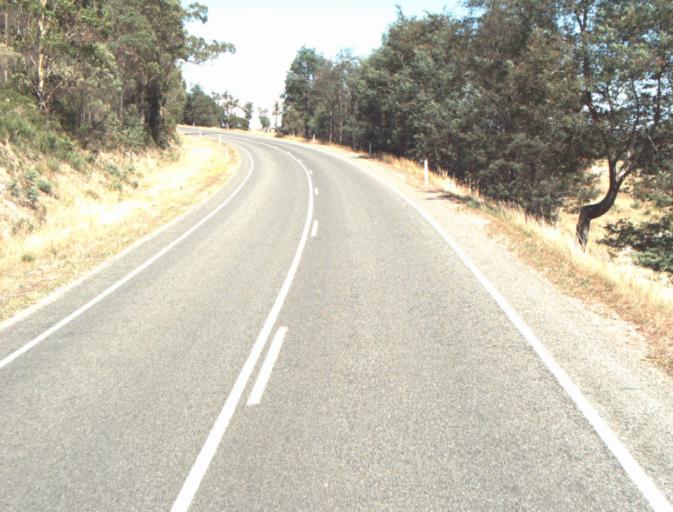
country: AU
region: Tasmania
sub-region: Dorset
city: Scottsdale
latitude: -41.3190
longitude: 147.3643
